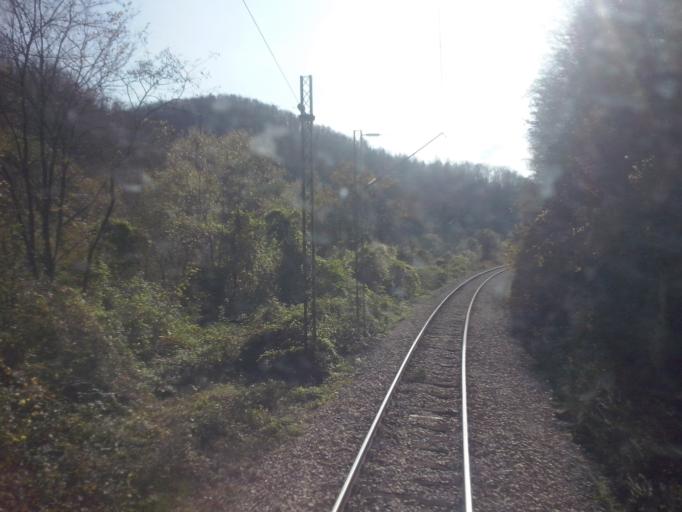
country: RS
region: Central Serbia
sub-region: Zlatiborski Okrug
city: Kosjeric
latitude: 43.9481
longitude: 19.9855
